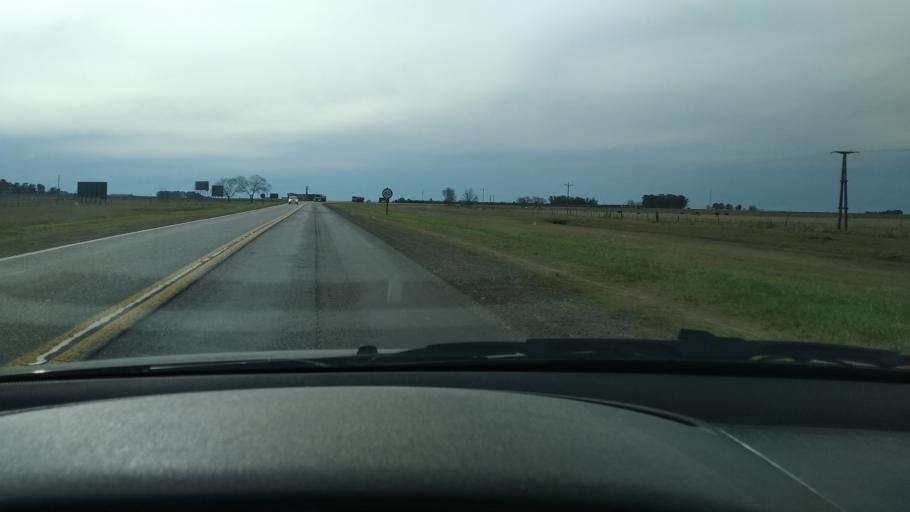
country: AR
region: Buenos Aires
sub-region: Partido de Azul
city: Azul
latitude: -36.7552
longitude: -59.8048
